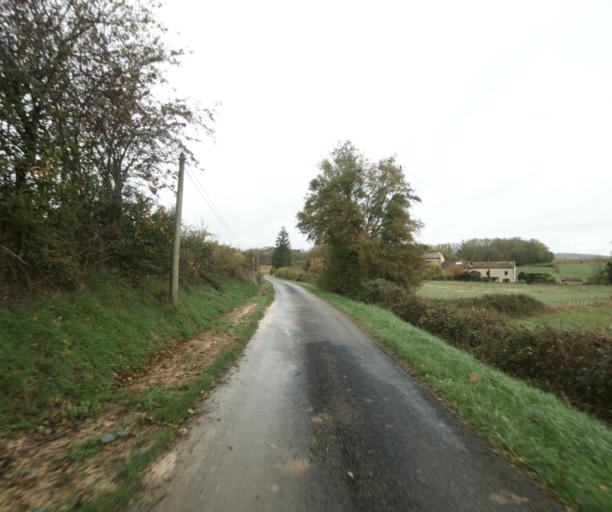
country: FR
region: Rhone-Alpes
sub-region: Departement de l'Ain
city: Pont-de-Vaux
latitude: 46.4810
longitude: 4.8797
